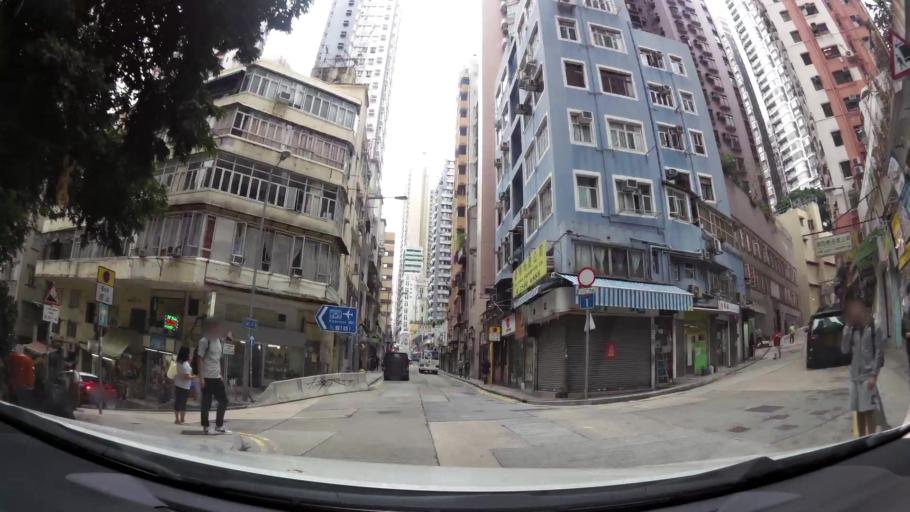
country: HK
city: Hong Kong
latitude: 22.2858
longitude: 114.1386
